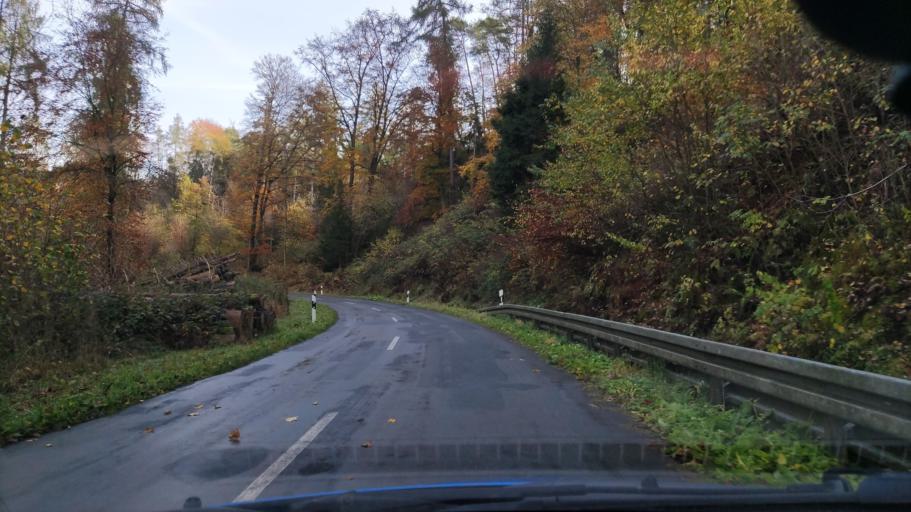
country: DE
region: Lower Saxony
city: Holenberg
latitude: 51.8923
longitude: 9.5913
